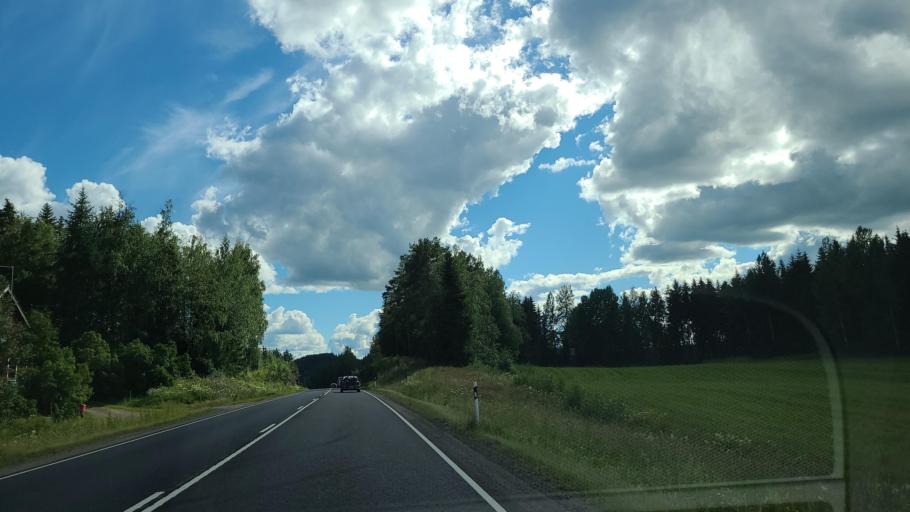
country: FI
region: Central Finland
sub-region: Jaemsae
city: Jaemsae
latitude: 61.9424
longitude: 25.3531
